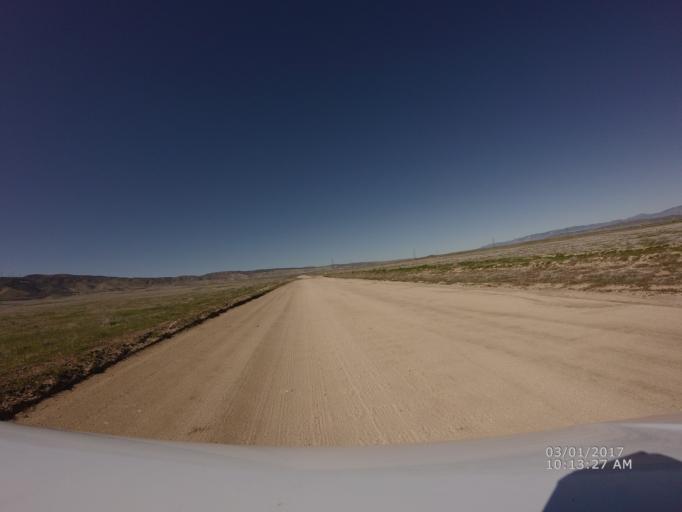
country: US
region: California
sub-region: Los Angeles County
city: Leona Valley
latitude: 34.6891
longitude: -118.3429
